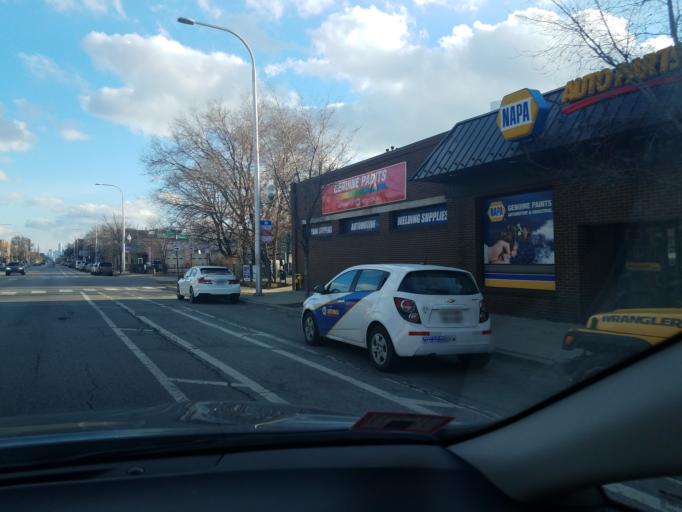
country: US
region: Illinois
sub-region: Cook County
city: Lincolnwood
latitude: 41.9590
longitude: -87.7269
